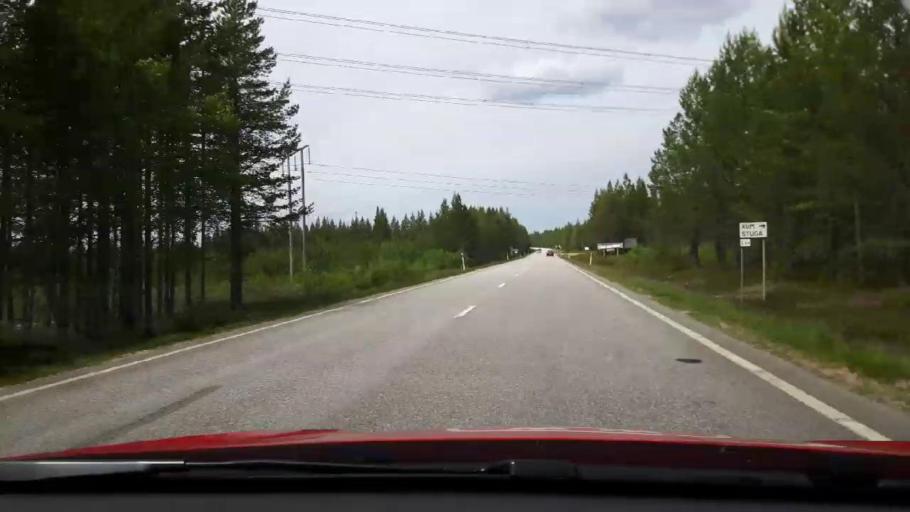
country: SE
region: Jaemtland
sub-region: Harjedalens Kommun
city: Sveg
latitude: 62.0547
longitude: 14.3037
